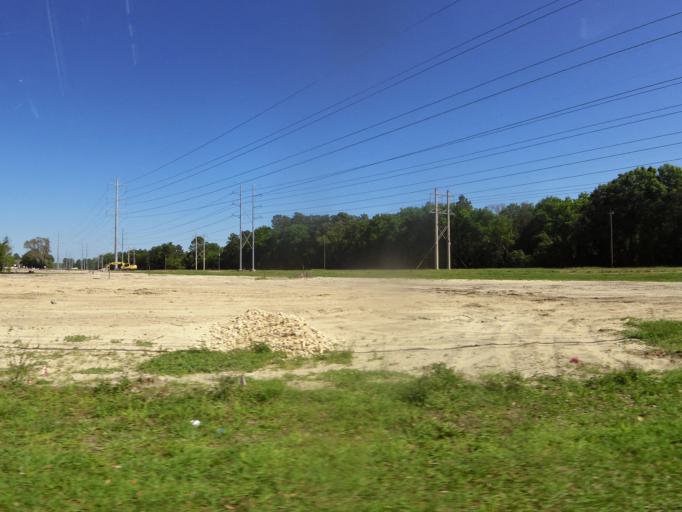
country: US
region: Florida
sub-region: Duval County
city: Jacksonville
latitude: 30.4559
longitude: -81.5956
